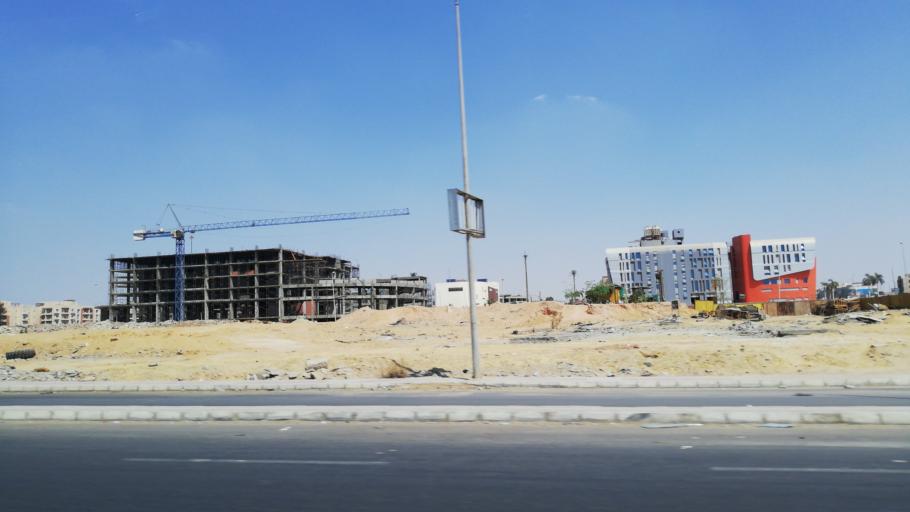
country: EG
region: Muhafazat al Qalyubiyah
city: Al Khankah
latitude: 30.0267
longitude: 31.4751
